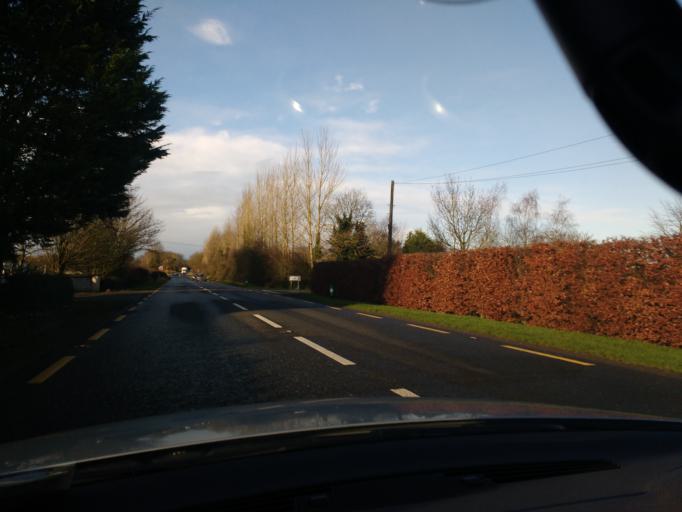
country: IE
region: Munster
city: Thurles
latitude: 52.6452
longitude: -7.7913
